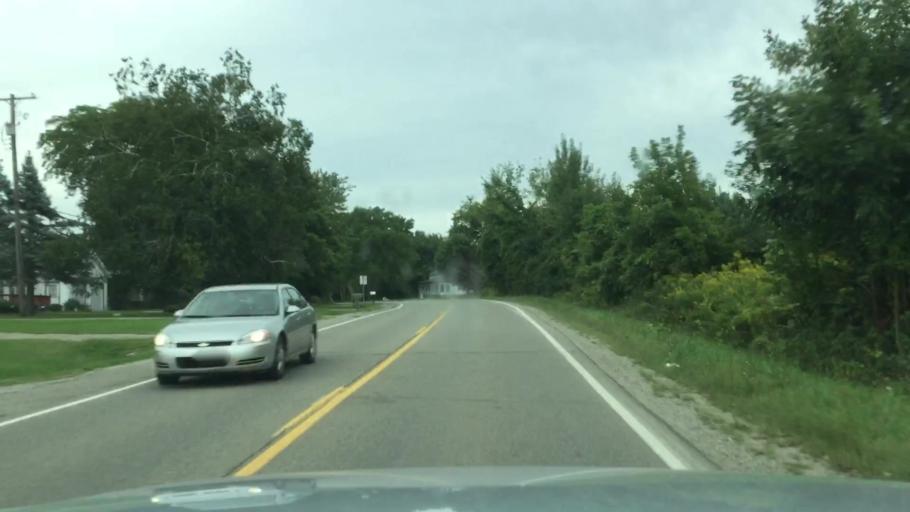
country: US
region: Michigan
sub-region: Genesee County
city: Argentine
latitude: 42.7935
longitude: -83.8530
